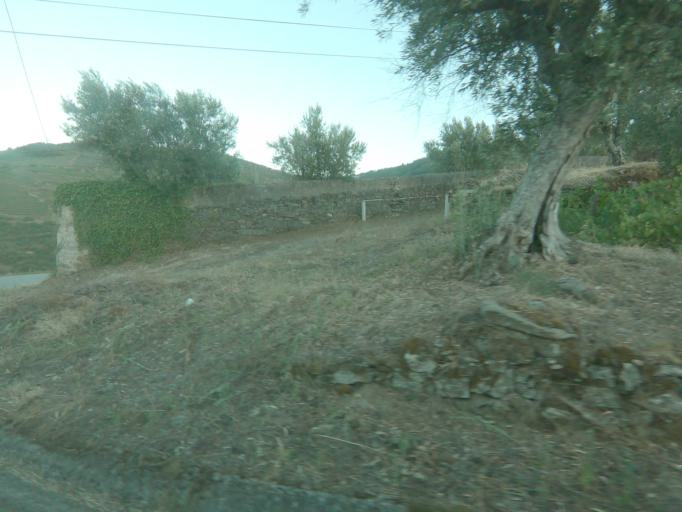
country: PT
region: Vila Real
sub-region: Peso da Regua
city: Peso da Regua
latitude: 41.1414
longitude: -7.7405
